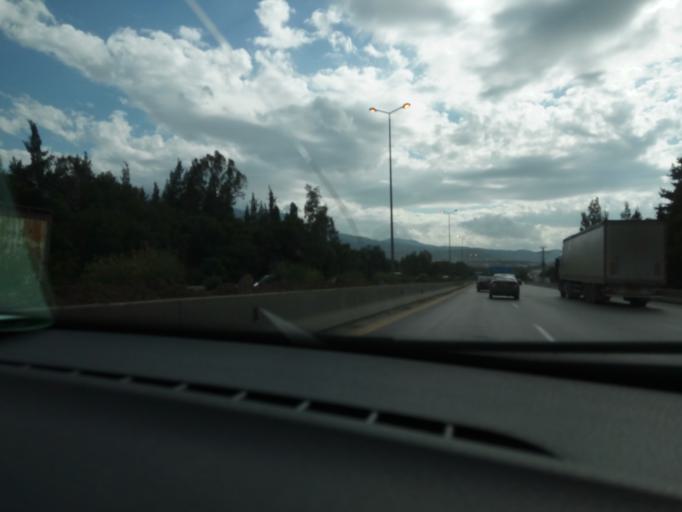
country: DZ
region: Blida
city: Chiffa
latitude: 36.4674
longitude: 2.7646
